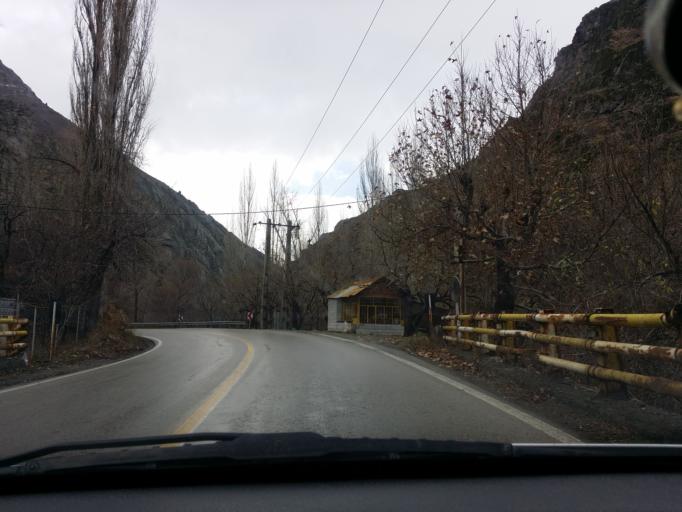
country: IR
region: Tehran
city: Tajrish
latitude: 36.0225
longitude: 51.2609
